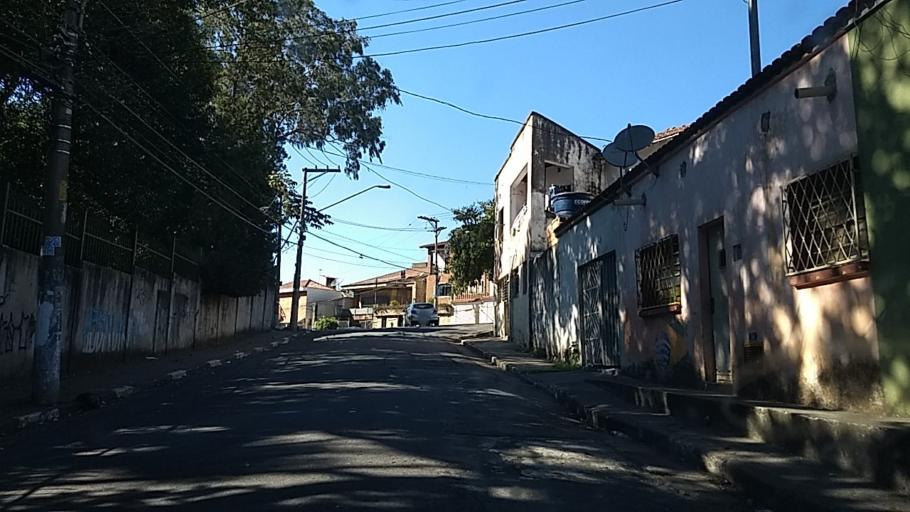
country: BR
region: Sao Paulo
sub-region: Guarulhos
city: Guarulhos
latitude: -23.5017
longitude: -46.5815
